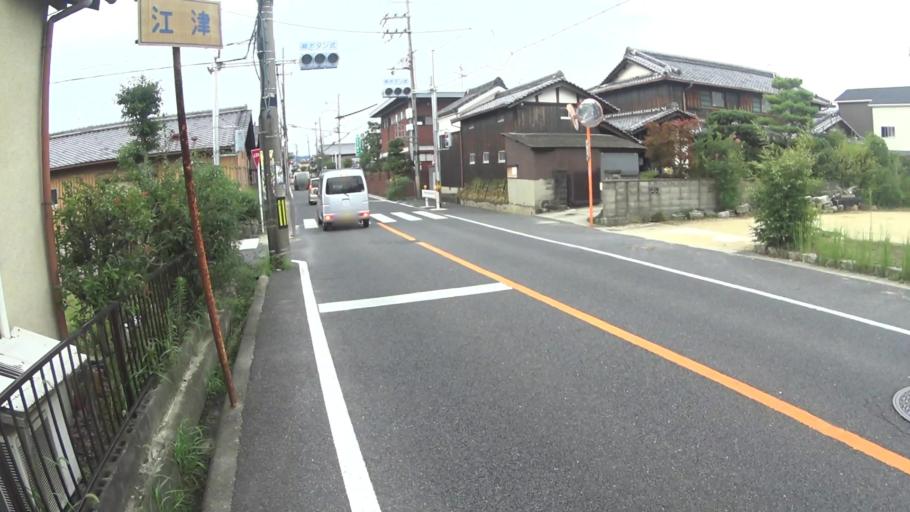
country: JP
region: Kyoto
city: Tanabe
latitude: 34.7609
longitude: 135.7914
